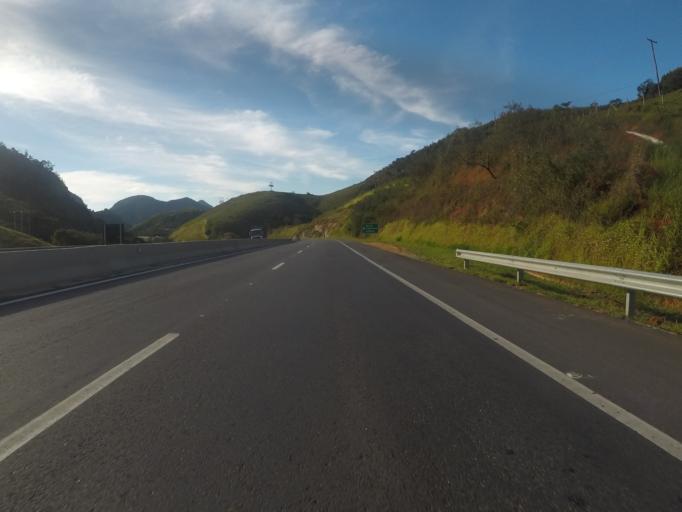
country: BR
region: Espirito Santo
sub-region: Ibiracu
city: Ibiracu
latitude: -19.8558
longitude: -40.3825
